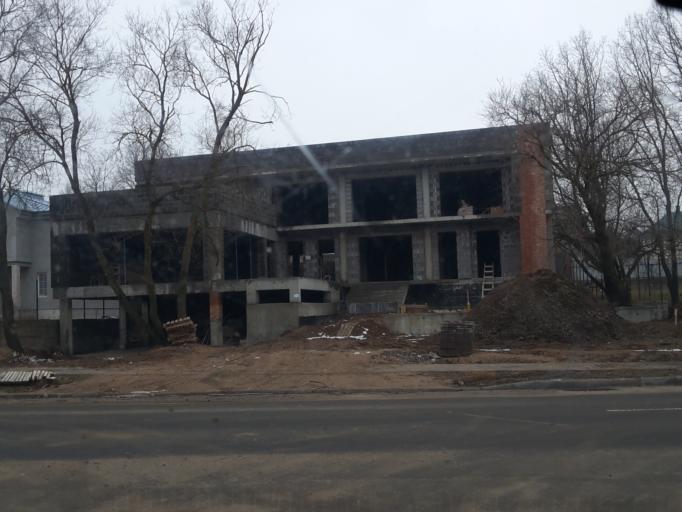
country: BY
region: Minsk
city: Zhdanovichy
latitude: 53.9206
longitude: 27.4053
